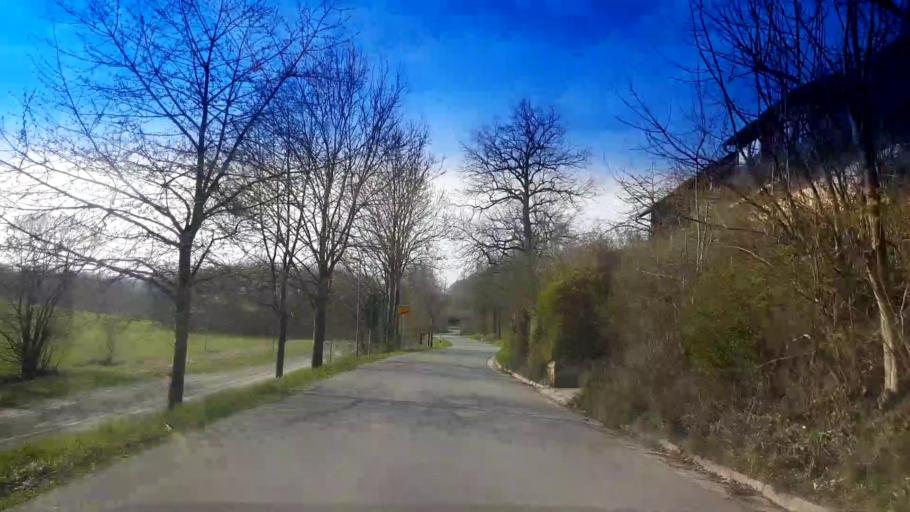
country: DE
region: Bavaria
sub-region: Upper Franconia
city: Neudrossenfeld
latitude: 50.0517
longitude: 11.4963
